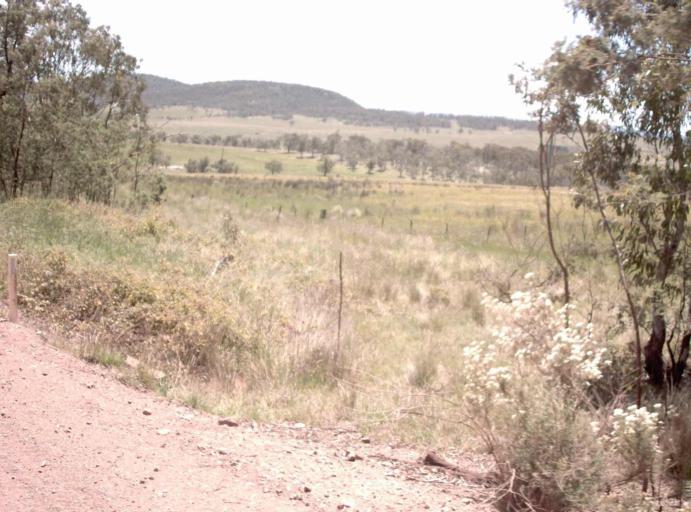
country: AU
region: New South Wales
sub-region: Snowy River
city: Jindabyne
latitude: -37.0285
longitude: 148.2734
